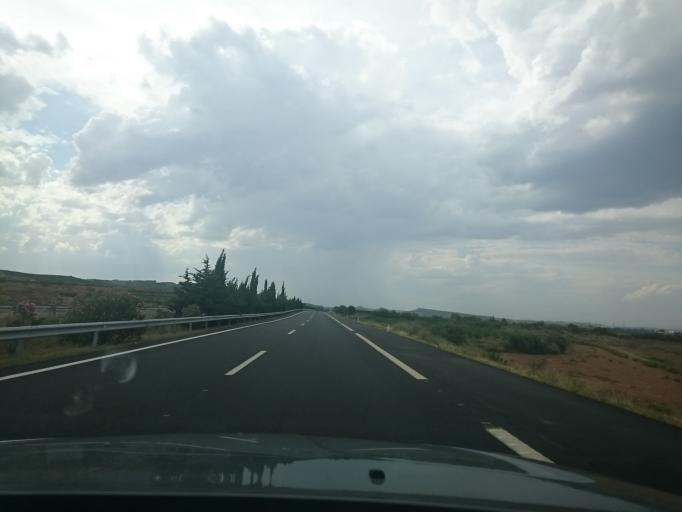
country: ES
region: La Rioja
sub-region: Provincia de La Rioja
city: Aldeanueva de Ebro
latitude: 42.2495
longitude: -1.9080
